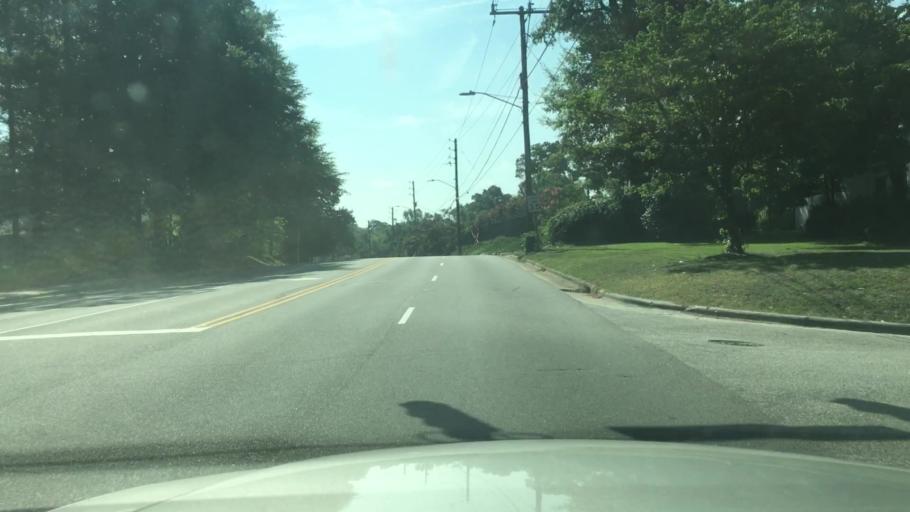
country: US
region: North Carolina
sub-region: Cumberland County
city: Fayetteville
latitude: 35.0609
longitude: -78.9165
